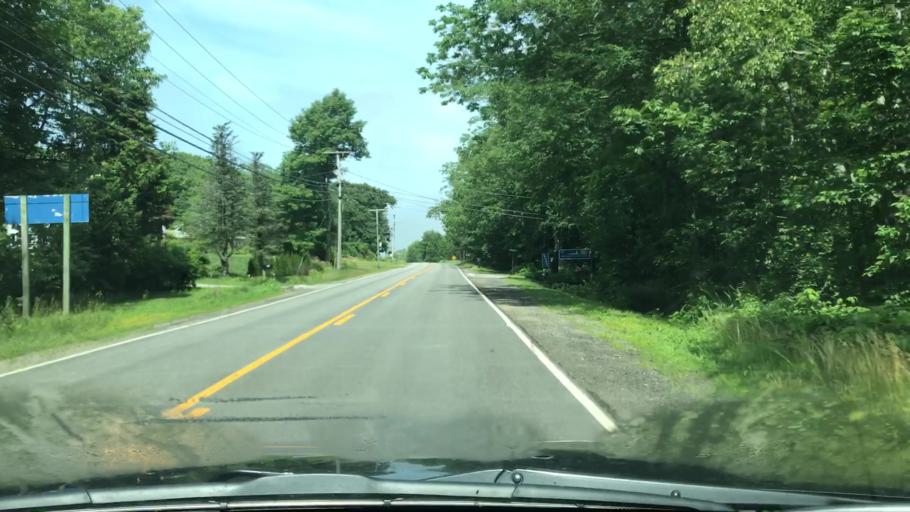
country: US
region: Maine
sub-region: Waldo County
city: Lincolnville
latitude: 44.2664
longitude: -69.0181
